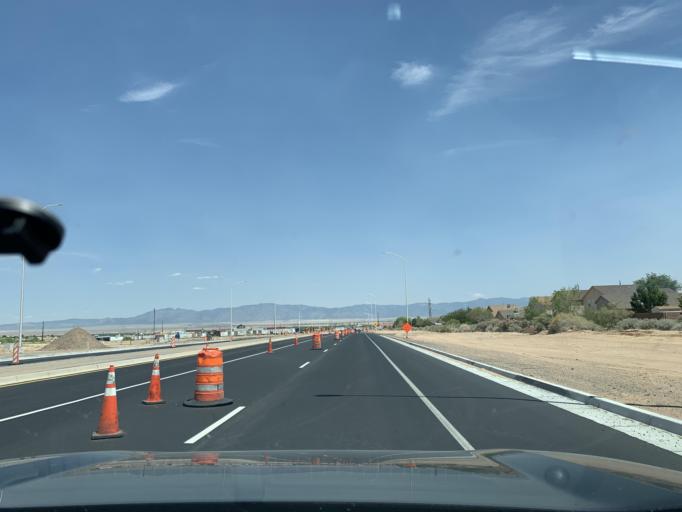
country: US
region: New Mexico
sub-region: Valencia County
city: Los Lunas
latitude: 34.8186
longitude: -106.7754
